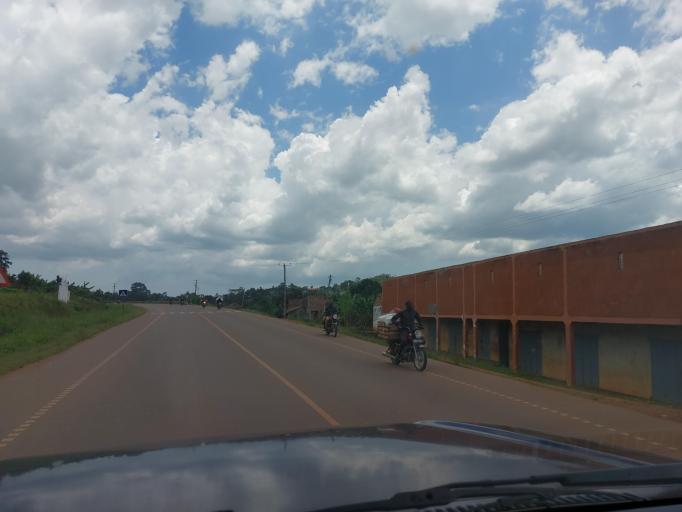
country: UG
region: Central Region
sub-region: Mukono District
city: Mukono
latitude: 0.3246
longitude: 32.7651
